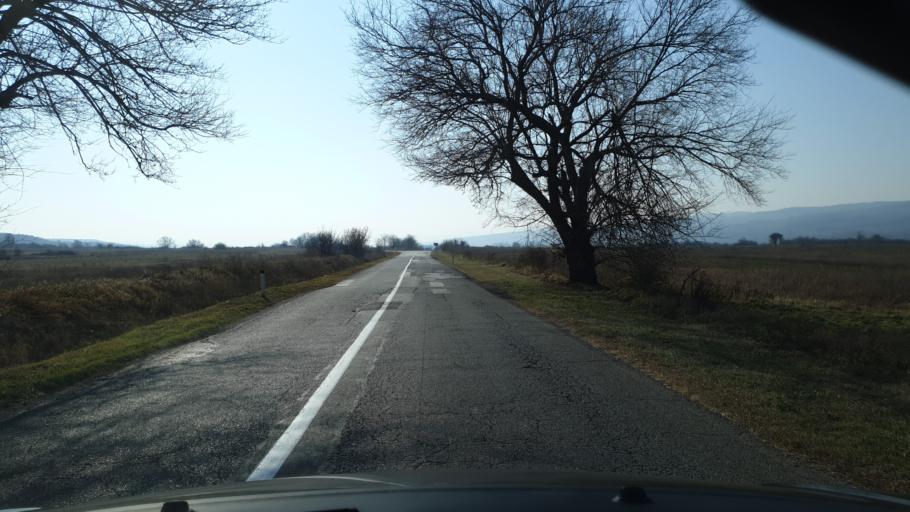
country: RS
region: Central Serbia
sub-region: Zajecarski Okrug
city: Knjazevac
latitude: 43.6626
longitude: 22.2865
